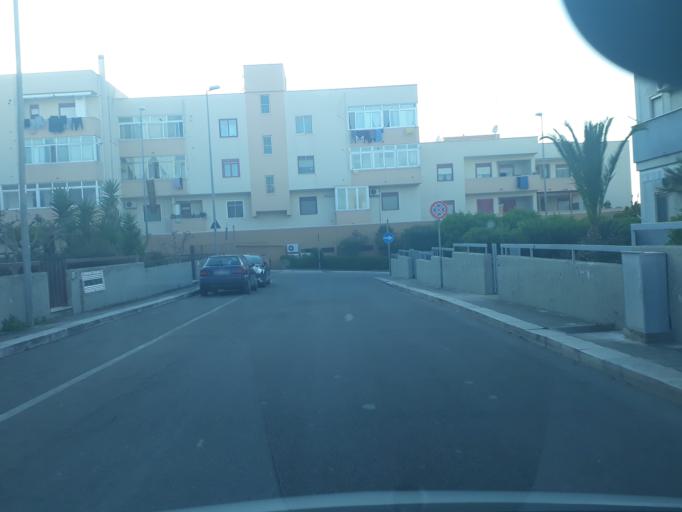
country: IT
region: Apulia
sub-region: Provincia di Bari
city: Locorotondo
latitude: 40.7588
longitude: 17.3306
